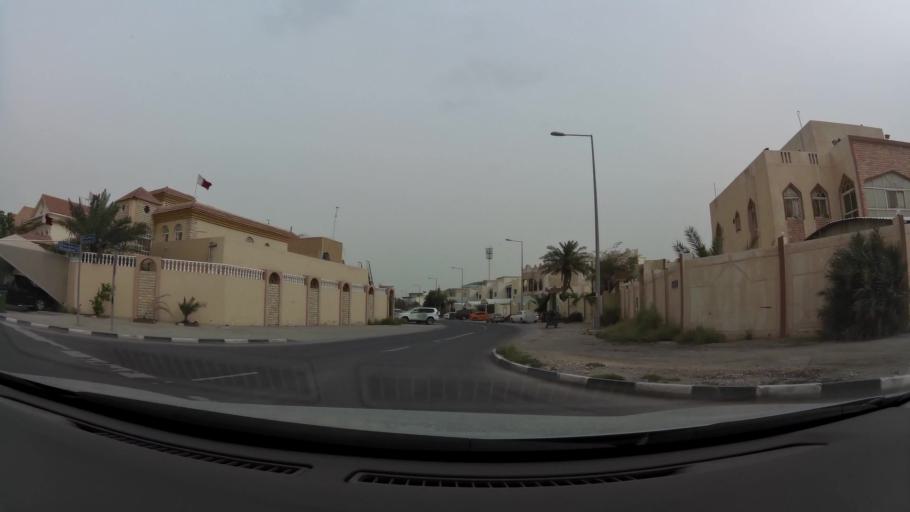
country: QA
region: Baladiyat ad Dawhah
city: Doha
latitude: 25.2507
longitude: 51.5042
